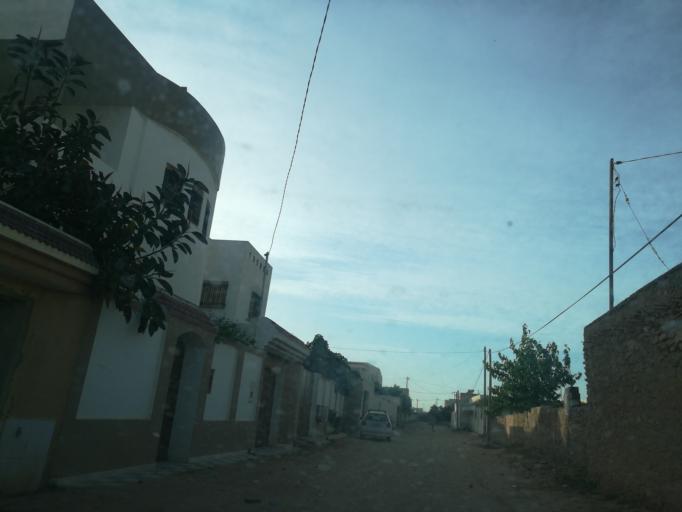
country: TN
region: Safaqis
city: Al Qarmadah
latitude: 34.8145
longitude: 10.7526
